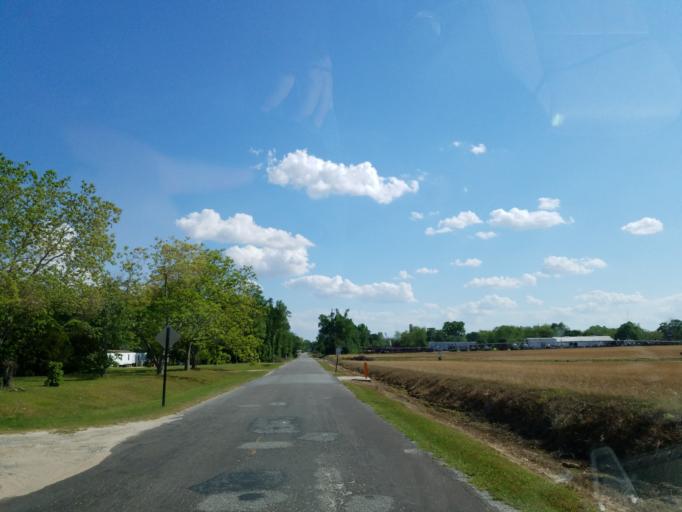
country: US
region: Georgia
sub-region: Dooly County
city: Unadilla
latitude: 32.2014
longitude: -83.7597
